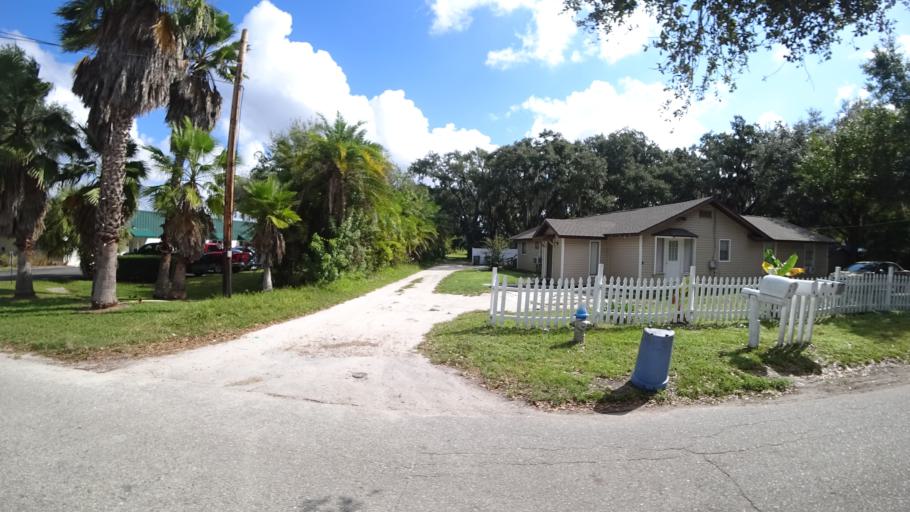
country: US
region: Florida
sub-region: Manatee County
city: Samoset
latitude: 27.4951
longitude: -82.5344
